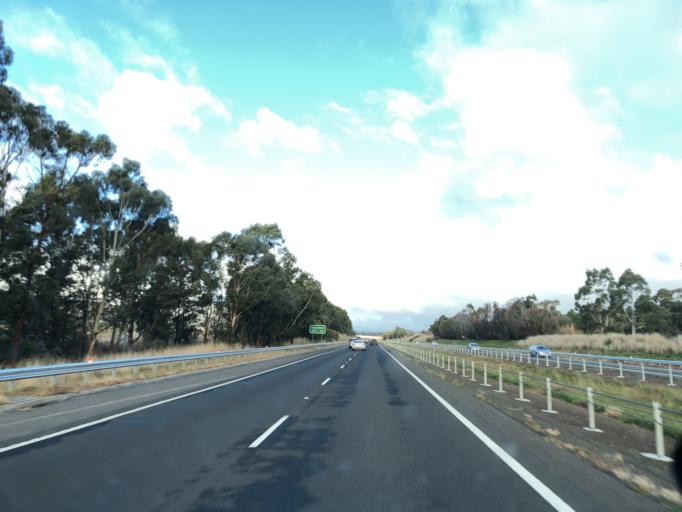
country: AU
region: Victoria
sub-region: Mount Alexander
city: Castlemaine
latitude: -37.2331
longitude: 144.4490
